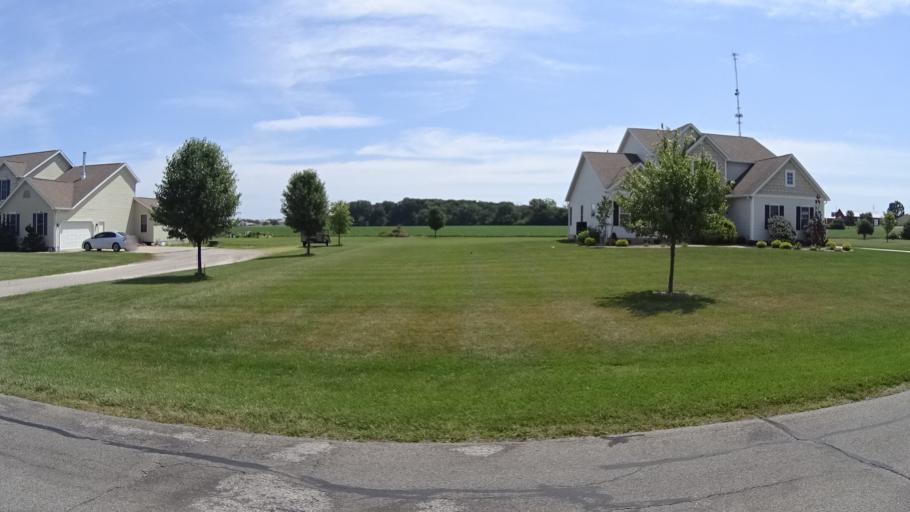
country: US
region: Ohio
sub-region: Erie County
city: Sandusky
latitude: 41.4076
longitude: -82.7885
